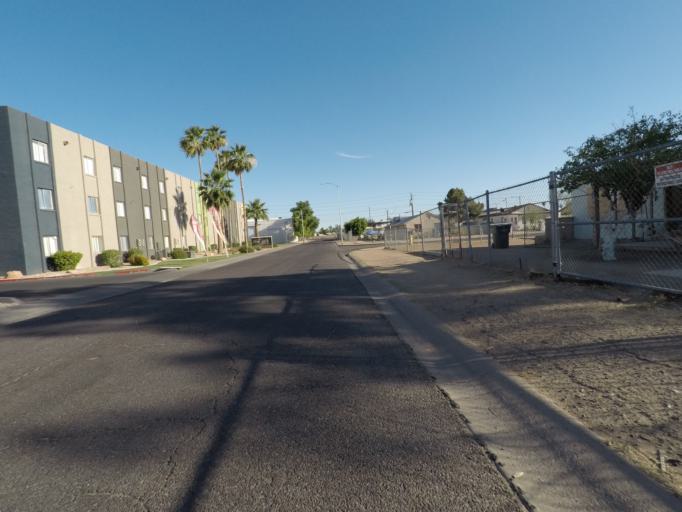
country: US
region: Arizona
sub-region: Maricopa County
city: Glendale
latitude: 33.5727
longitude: -112.0956
